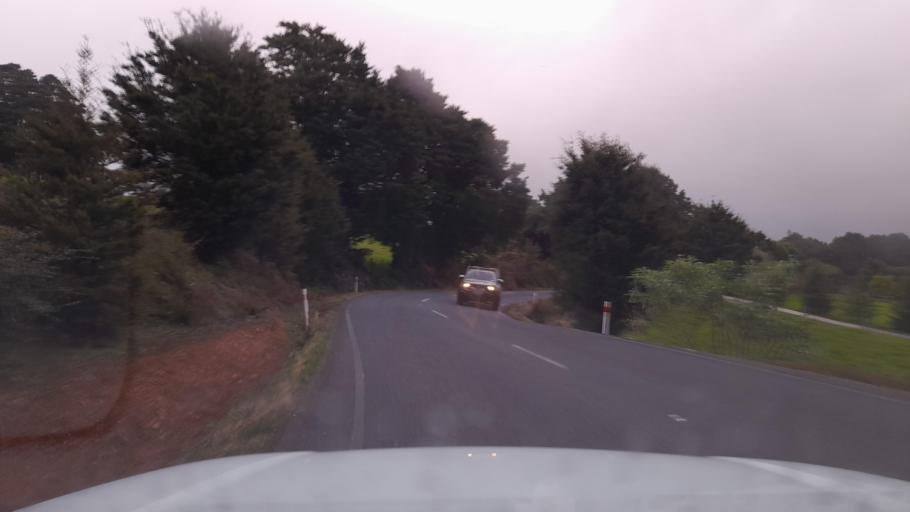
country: NZ
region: Northland
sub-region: Whangarei
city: Maungatapere
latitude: -35.6952
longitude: 174.1859
